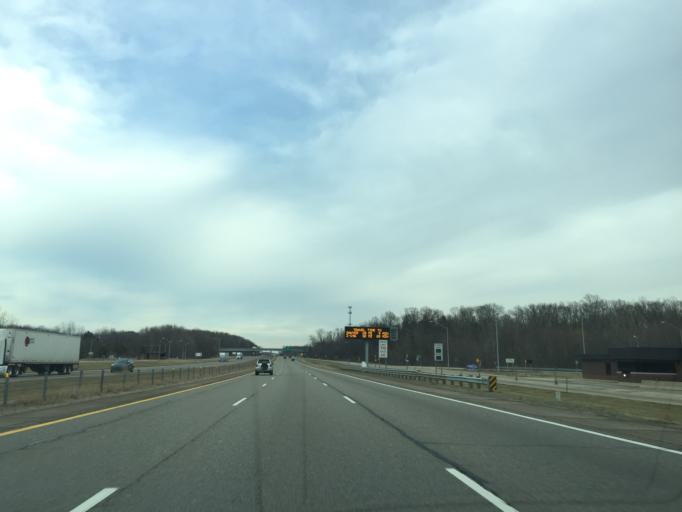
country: US
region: Michigan
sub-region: Berrien County
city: New Buffalo
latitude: 41.7842
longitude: -86.7194
